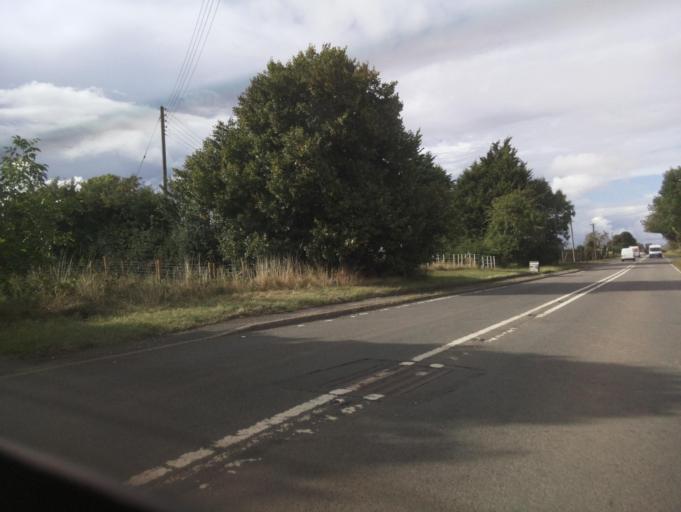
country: GB
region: England
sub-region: Telford and Wrekin
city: Madeley
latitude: 52.6121
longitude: -2.4115
